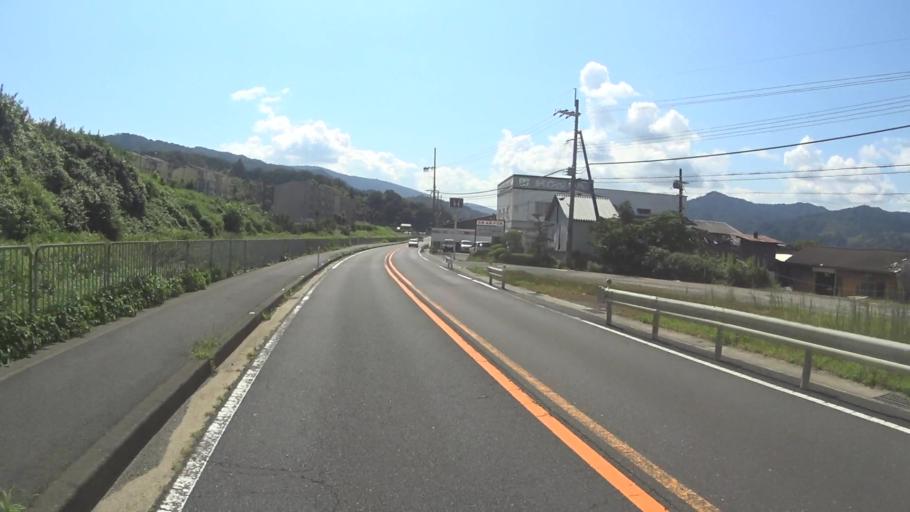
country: JP
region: Kyoto
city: Miyazu
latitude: 35.5445
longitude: 135.2105
